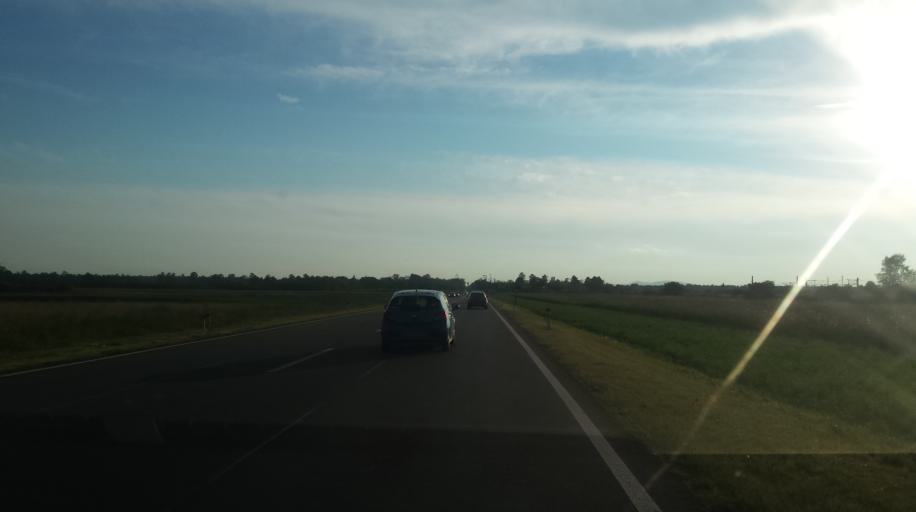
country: AT
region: Lower Austria
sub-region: Politischer Bezirk Ganserndorf
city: Parbasdorf
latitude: 48.3106
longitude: 16.6017
